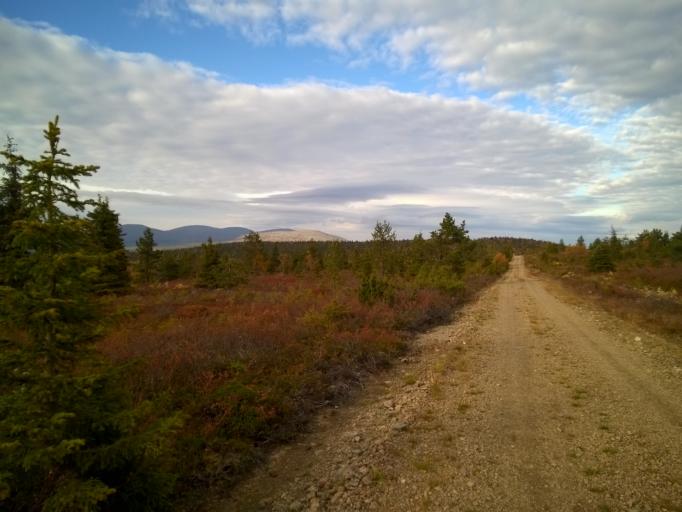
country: FI
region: Lapland
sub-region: Tunturi-Lappi
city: Muonio
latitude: 67.9762
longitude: 24.1023
